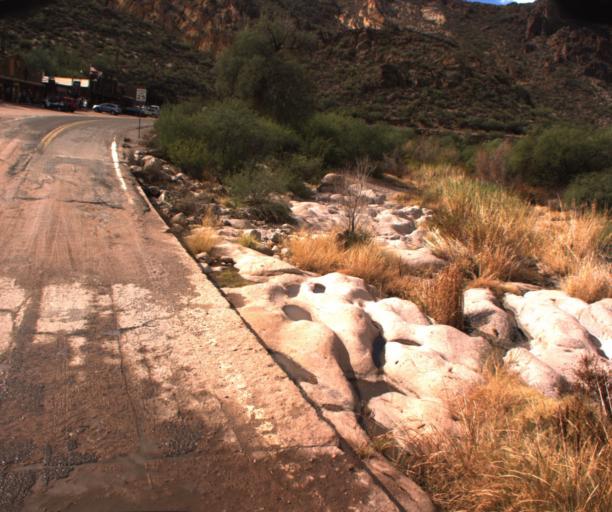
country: US
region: Arizona
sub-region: Pinal County
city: Apache Junction
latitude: 33.5271
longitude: -111.3893
